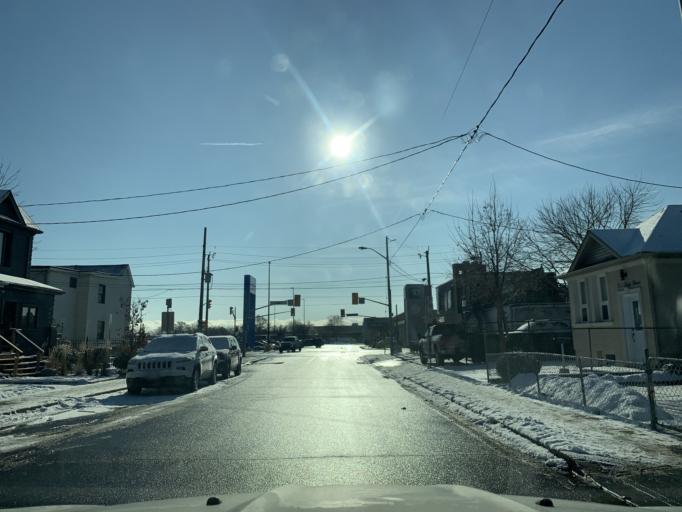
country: CA
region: Ontario
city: Toronto
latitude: 43.6687
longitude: -79.4873
